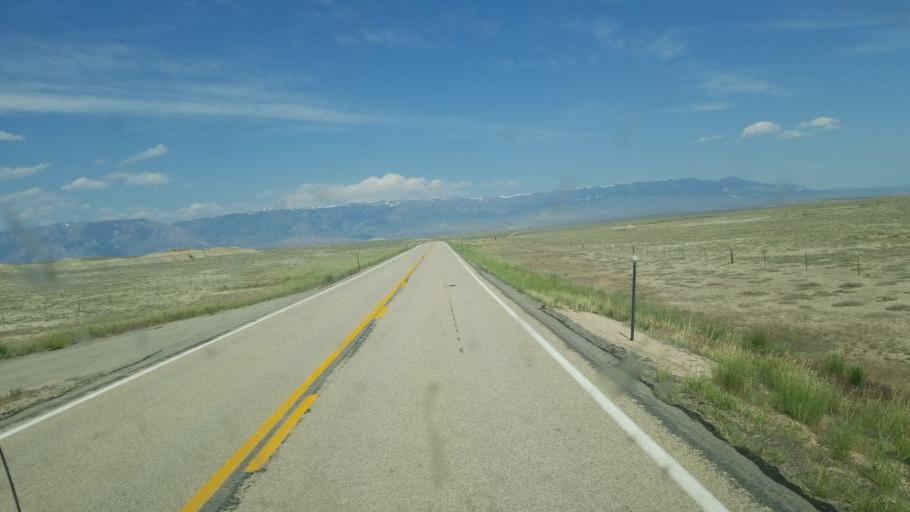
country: US
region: Wyoming
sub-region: Park County
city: Powell
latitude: 44.8437
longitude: -108.9951
